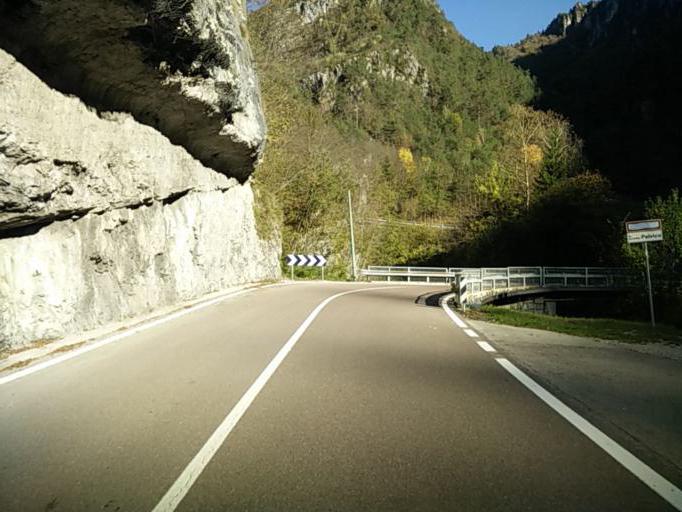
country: IT
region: Trentino-Alto Adige
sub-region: Provincia di Trento
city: Storo
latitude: 45.8436
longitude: 10.6197
